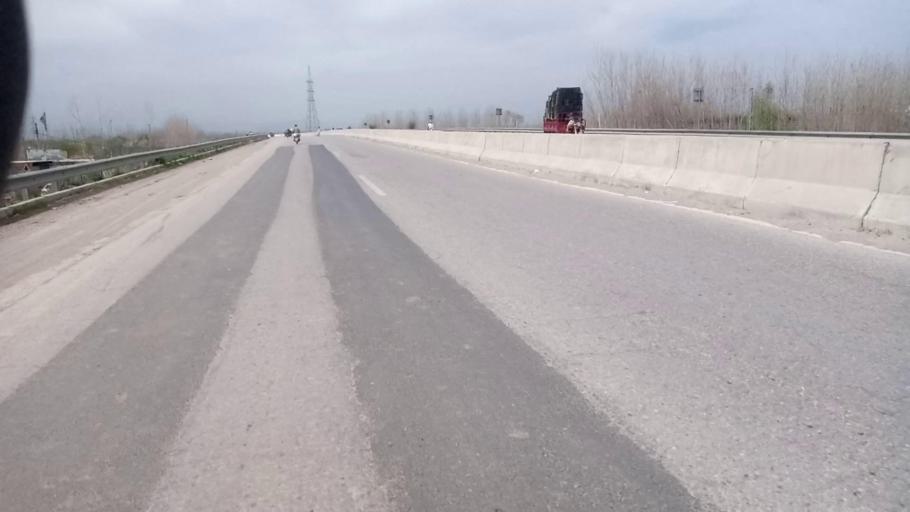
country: PK
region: Khyber Pakhtunkhwa
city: Peshawar
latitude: 34.0535
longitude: 71.6123
